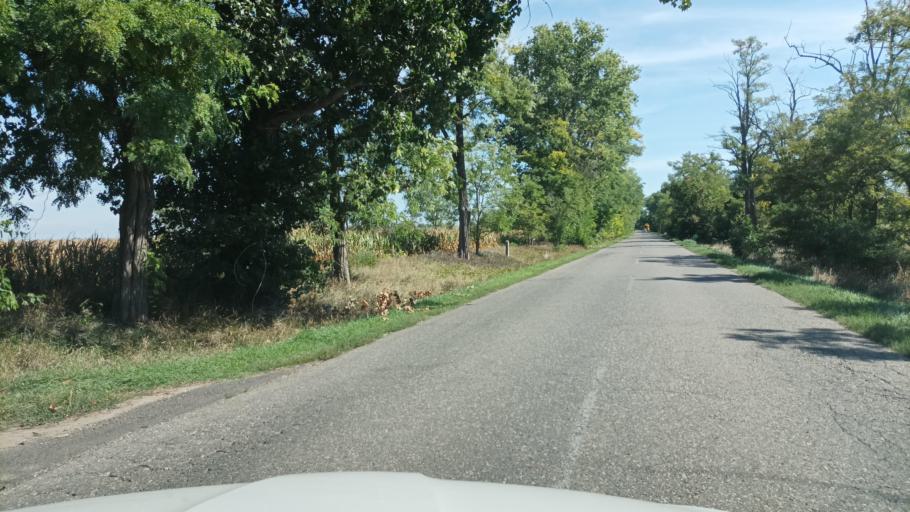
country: HU
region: Pest
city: Zsambok
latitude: 47.5515
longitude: 19.5895
